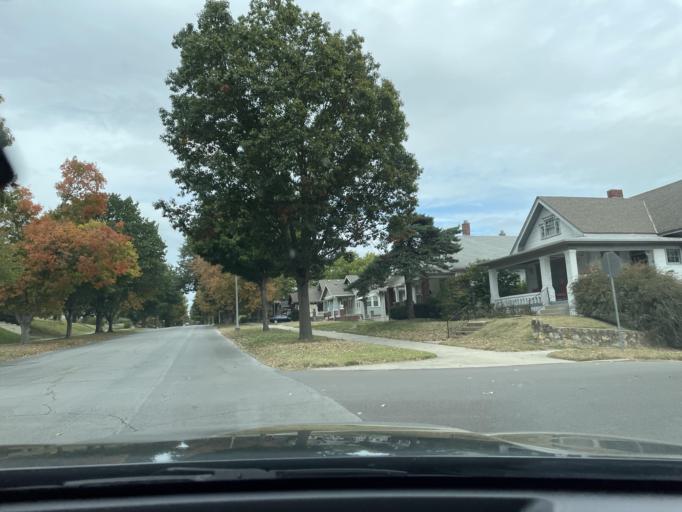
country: US
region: Missouri
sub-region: Buchanan County
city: Saint Joseph
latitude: 39.7702
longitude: -94.8248
